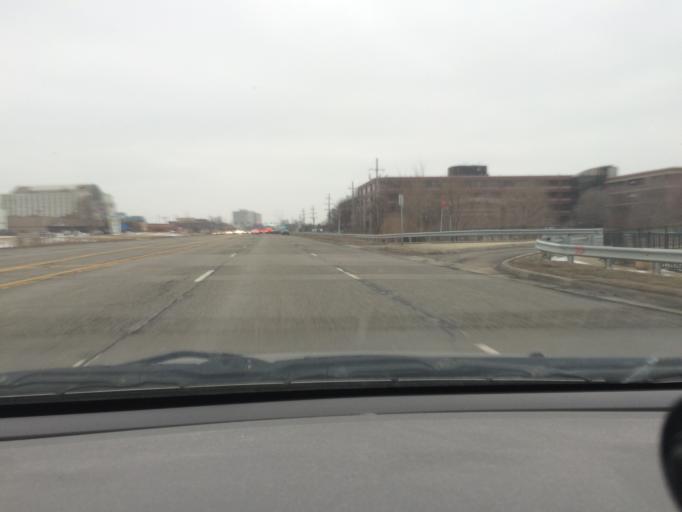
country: US
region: Illinois
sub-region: DuPage County
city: Oakbrook Terrace
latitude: 41.8412
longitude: -87.9955
